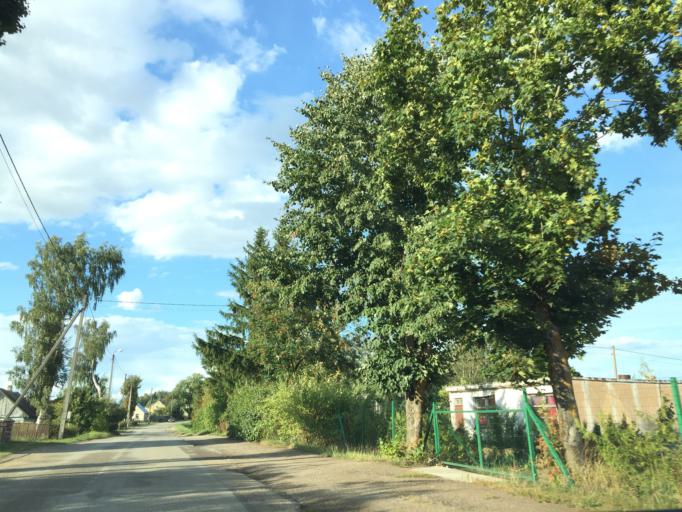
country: LT
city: Zagare
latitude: 56.3678
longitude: 23.2653
